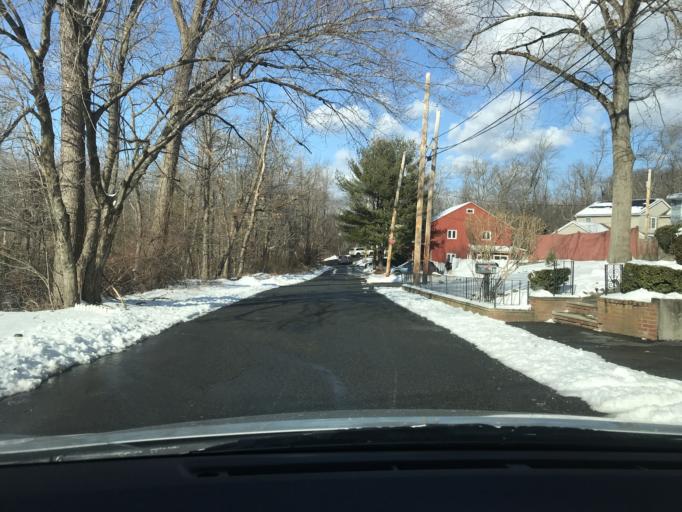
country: US
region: Massachusetts
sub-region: Essex County
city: Saugus
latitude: 42.4891
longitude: -71.0110
